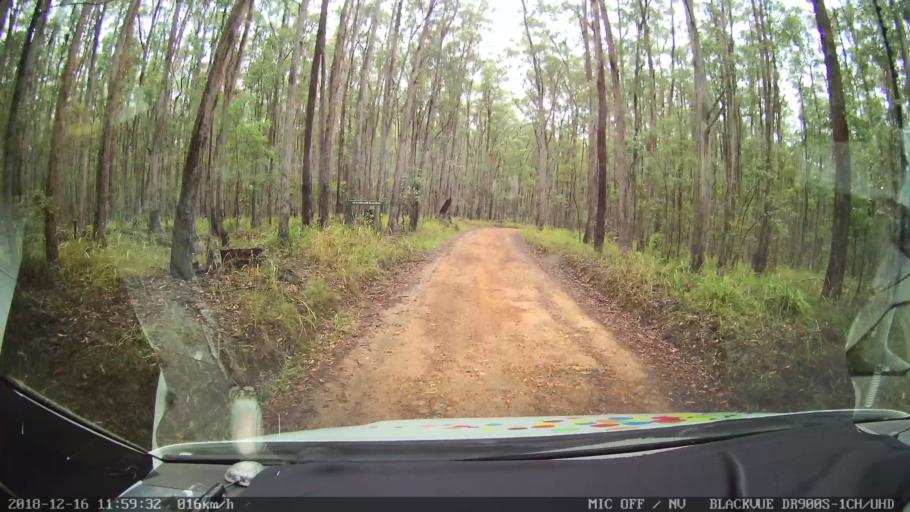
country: AU
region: New South Wales
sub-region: Tenterfield Municipality
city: Carrolls Creek
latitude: -28.9266
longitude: 152.3156
